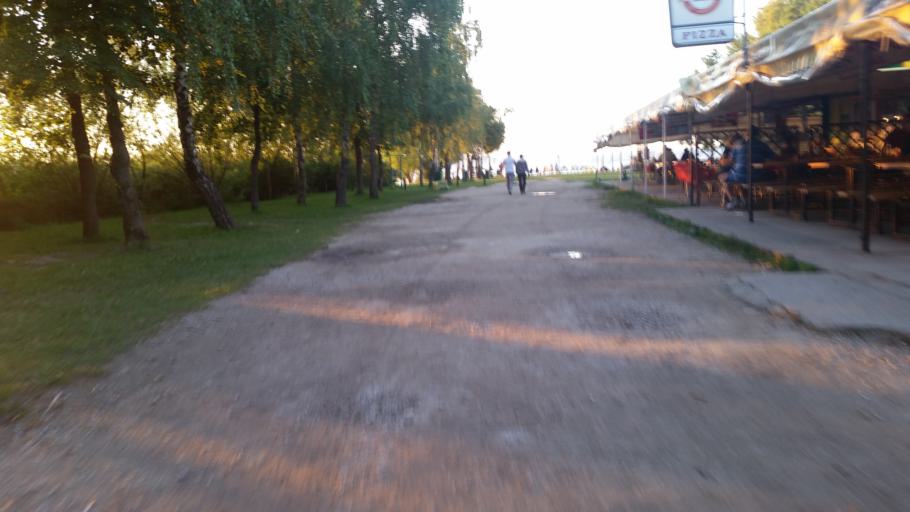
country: HU
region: Somogy
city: Zamardi
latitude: 46.8950
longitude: 17.9917
